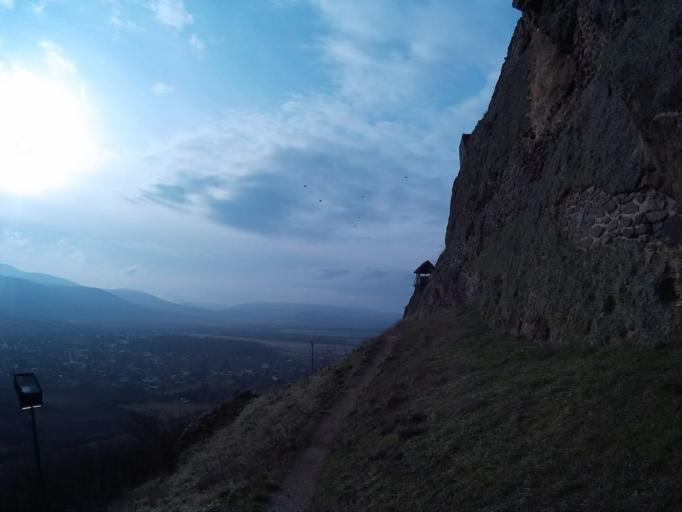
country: HU
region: Borsod-Abauj-Zemplen
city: Abaujszanto
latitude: 48.3447
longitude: 21.2326
